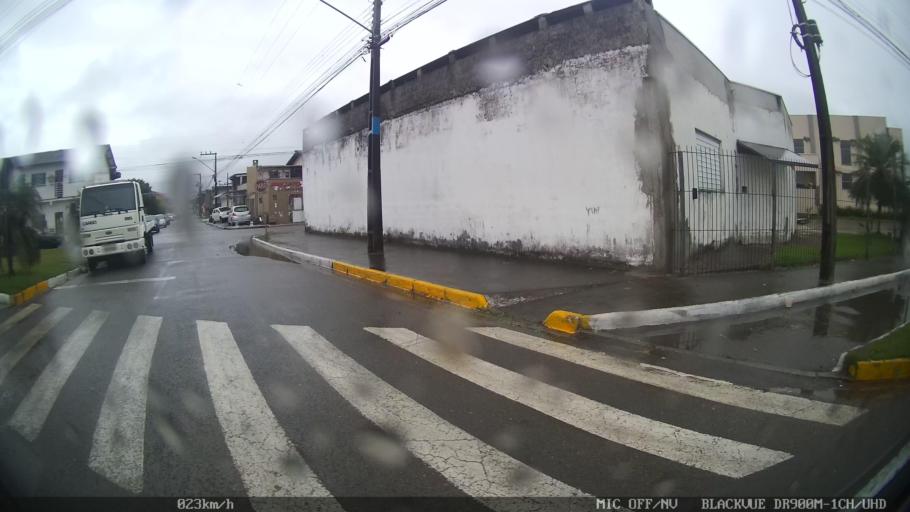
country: BR
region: Santa Catarina
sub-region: Itajai
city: Itajai
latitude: -26.9225
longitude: -48.6975
